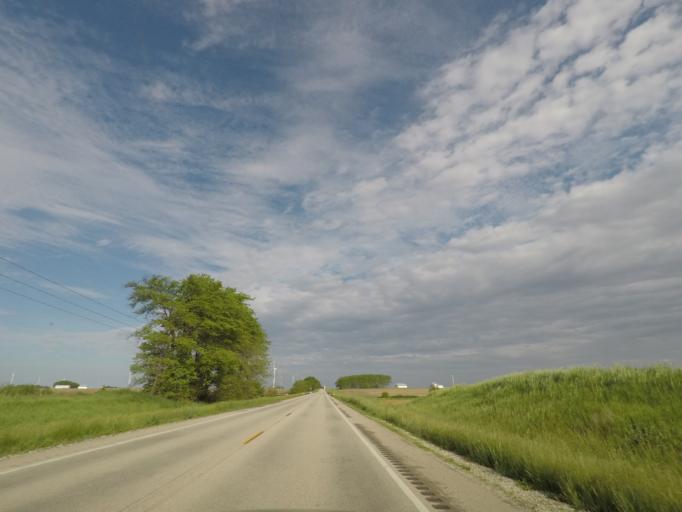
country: US
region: Illinois
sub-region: Logan County
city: Mount Pulaski
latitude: 39.9788
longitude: -89.2028
